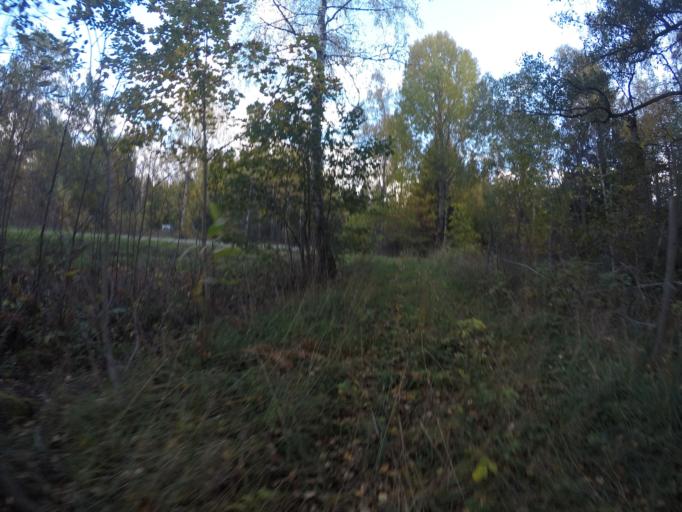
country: SE
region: Vaestmanland
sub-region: Arboga Kommun
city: Tyringe
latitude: 59.3322
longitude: 15.9683
